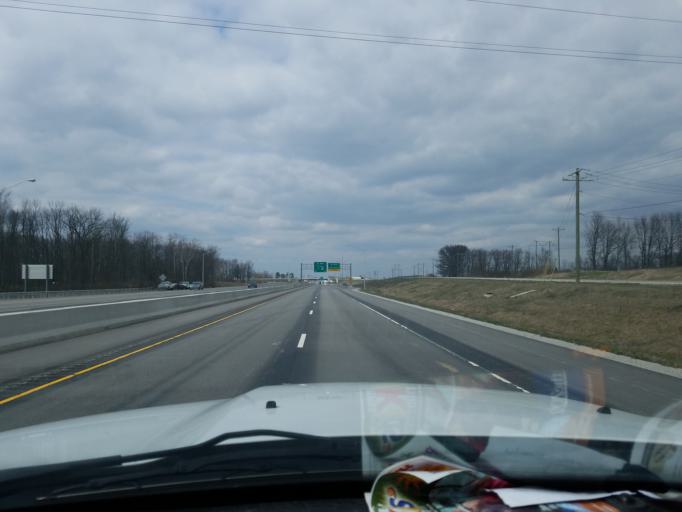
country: US
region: Indiana
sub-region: Vigo County
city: Terre Haute
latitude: 39.4229
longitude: -87.3329
